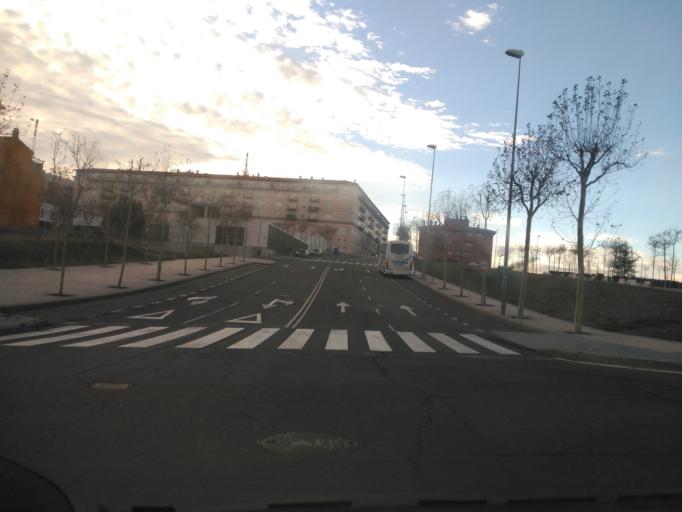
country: ES
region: Castille and Leon
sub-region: Provincia de Salamanca
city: Salamanca
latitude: 40.9810
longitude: -5.6693
